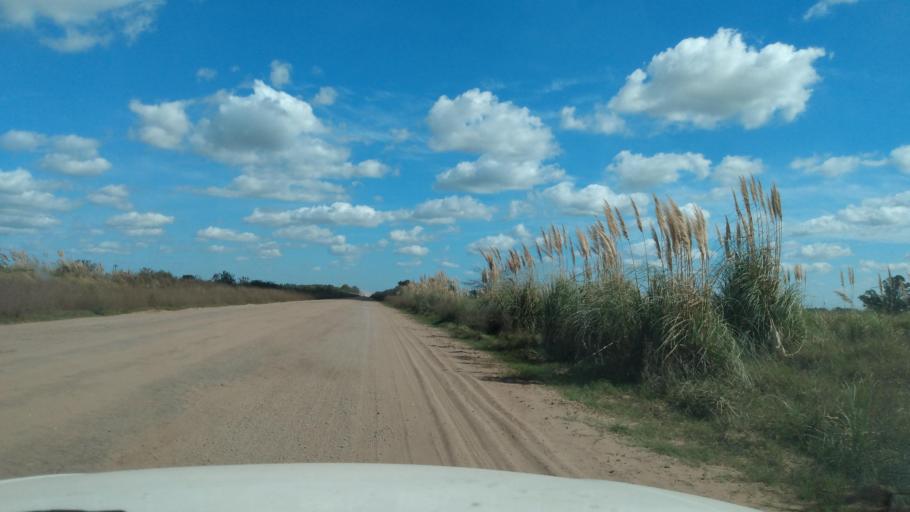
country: AR
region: Buenos Aires
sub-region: Partido de Navarro
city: Navarro
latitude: -35.0042
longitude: -59.3696
